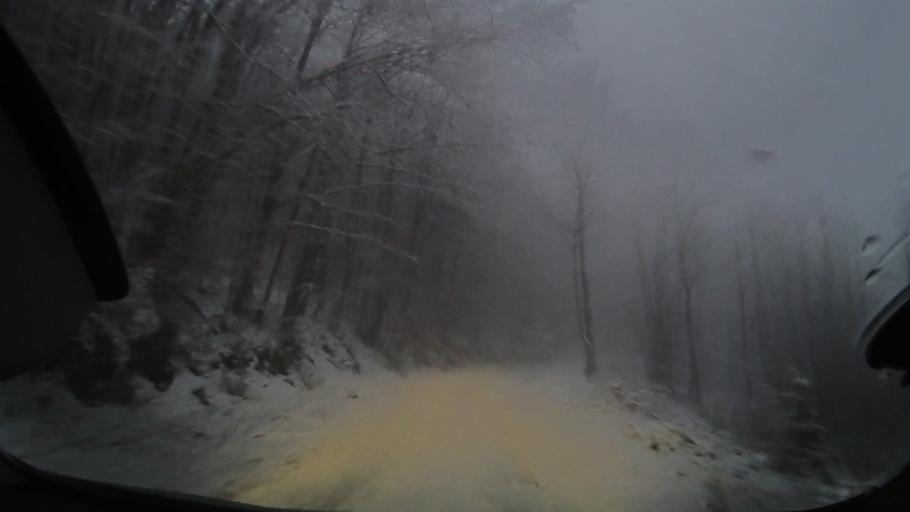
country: RO
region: Alba
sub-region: Comuna Avram Iancu
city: Avram Iancu
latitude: 46.3126
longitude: 22.8173
